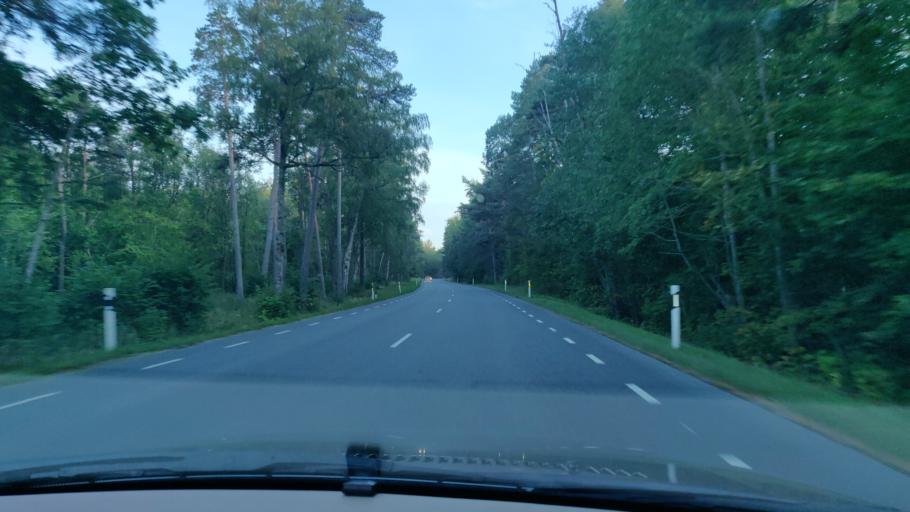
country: EE
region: Harju
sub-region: Paldiski linn
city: Paldiski
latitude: 59.3937
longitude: 24.2420
